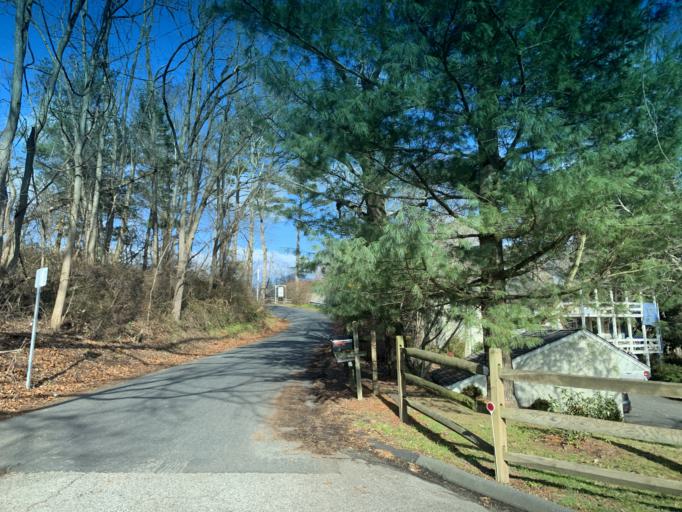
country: US
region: Maryland
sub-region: Harford County
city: Aberdeen
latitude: 39.5858
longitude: -76.2328
